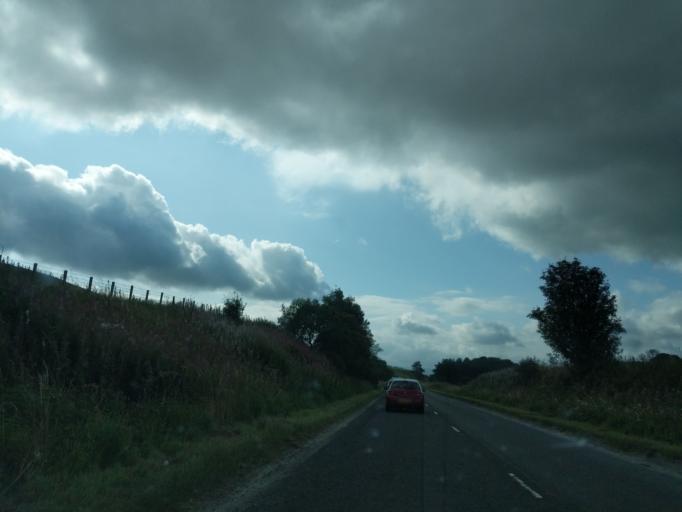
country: GB
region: Scotland
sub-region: Midlothian
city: Penicuik
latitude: 55.7574
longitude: -3.2067
